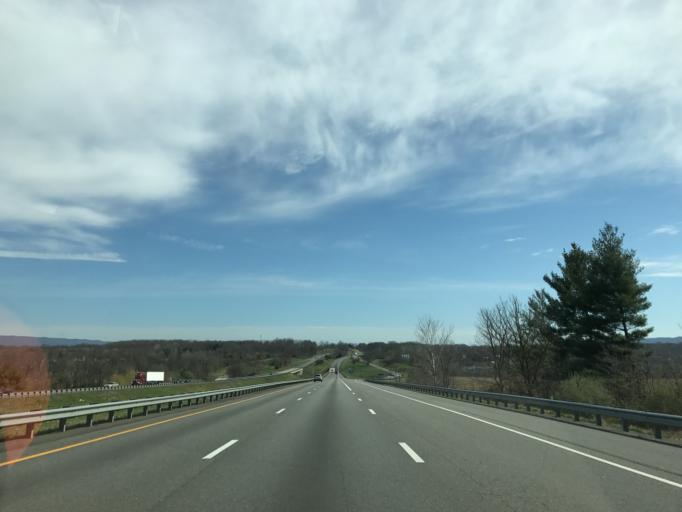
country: US
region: Virginia
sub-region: Shenandoah County
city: Edinburg
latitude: 38.8256
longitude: -78.5810
